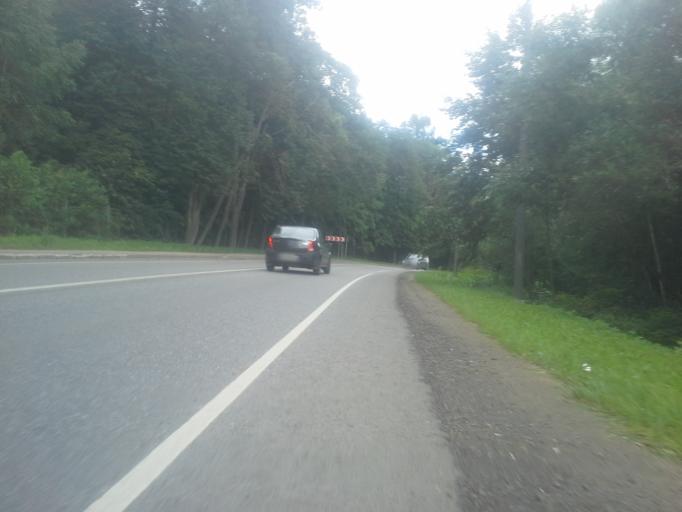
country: RU
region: Moskovskaya
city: Zvenigorod
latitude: 55.7323
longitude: 36.8306
